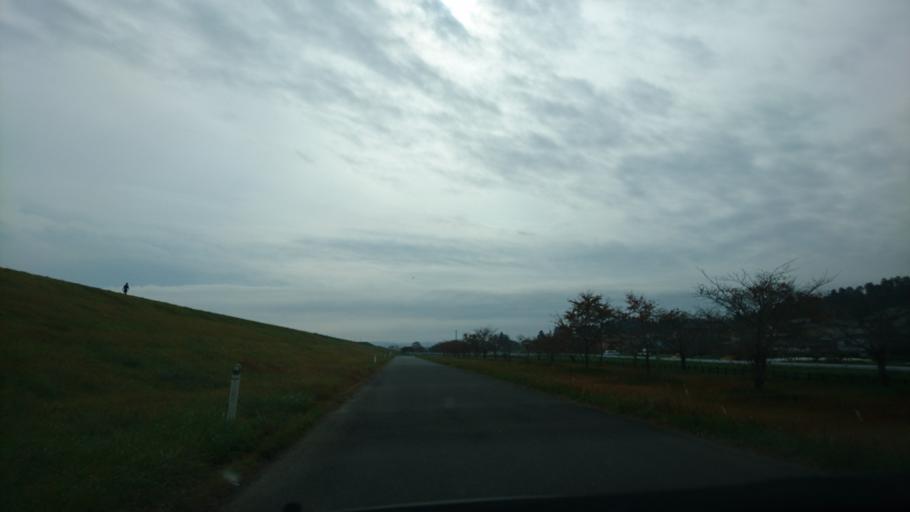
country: JP
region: Iwate
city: Ichinoseki
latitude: 38.9583
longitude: 141.1301
